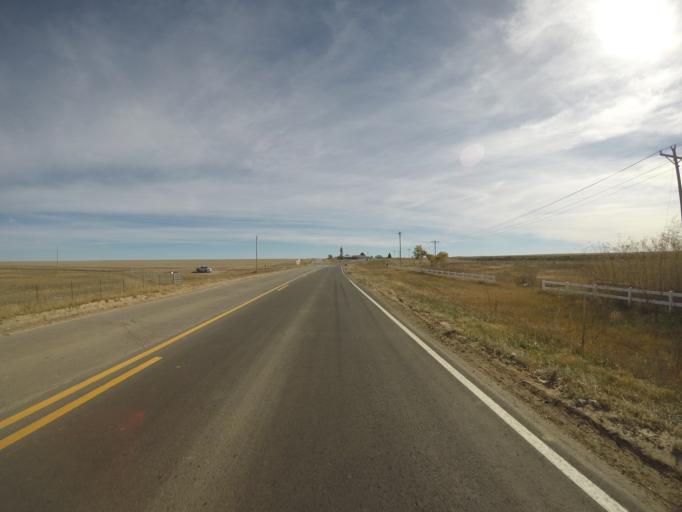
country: US
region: Colorado
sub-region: Adams County
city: Strasburg
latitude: 39.7385
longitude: -104.3038
